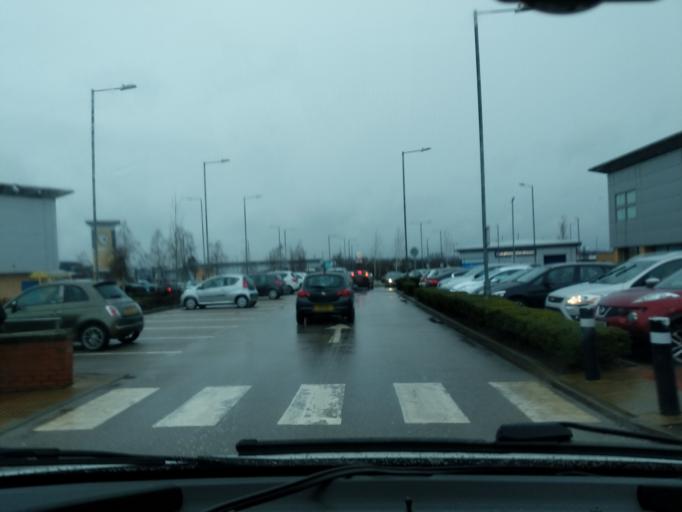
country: GB
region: England
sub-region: St. Helens
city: St Helens
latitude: 53.4437
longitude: -2.7325
